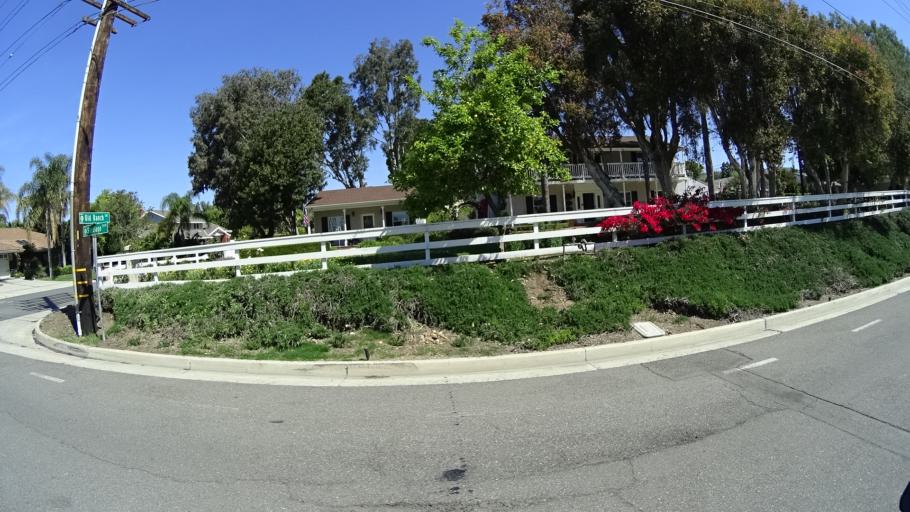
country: US
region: California
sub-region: Orange County
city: Villa Park
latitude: 33.8145
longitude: -117.8014
